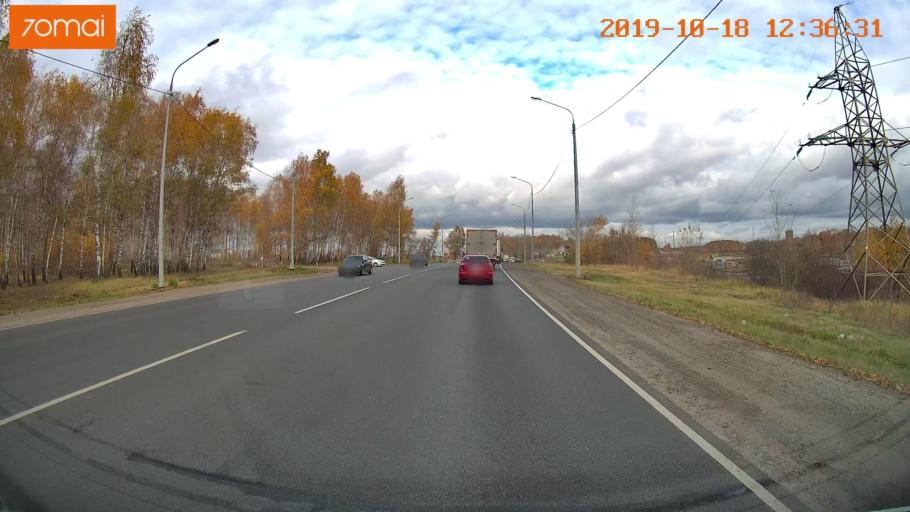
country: RU
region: Rjazan
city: Ryazan'
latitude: 54.6360
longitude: 39.6340
